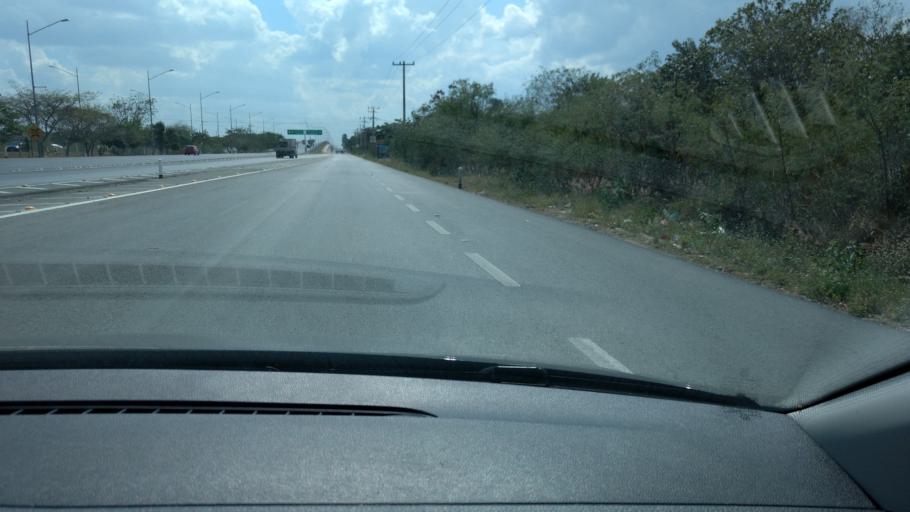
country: MX
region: Yucatan
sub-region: Kanasin
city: Kanasin
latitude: 20.9879
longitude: -89.5632
